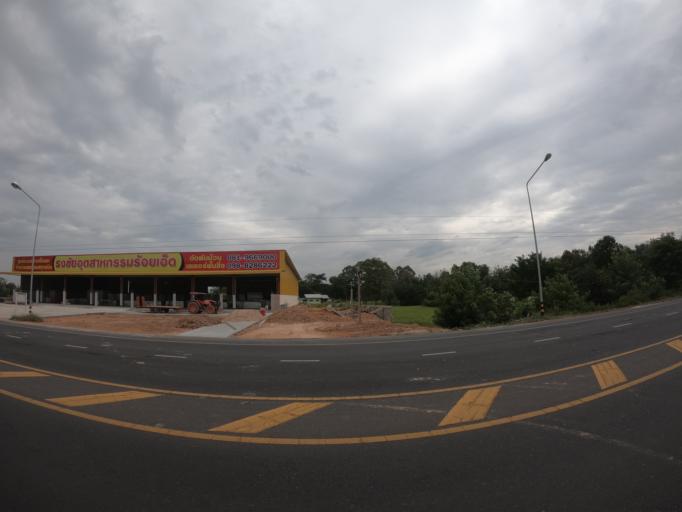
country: TH
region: Roi Et
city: Thawat Buri
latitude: 16.0842
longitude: 103.7476
